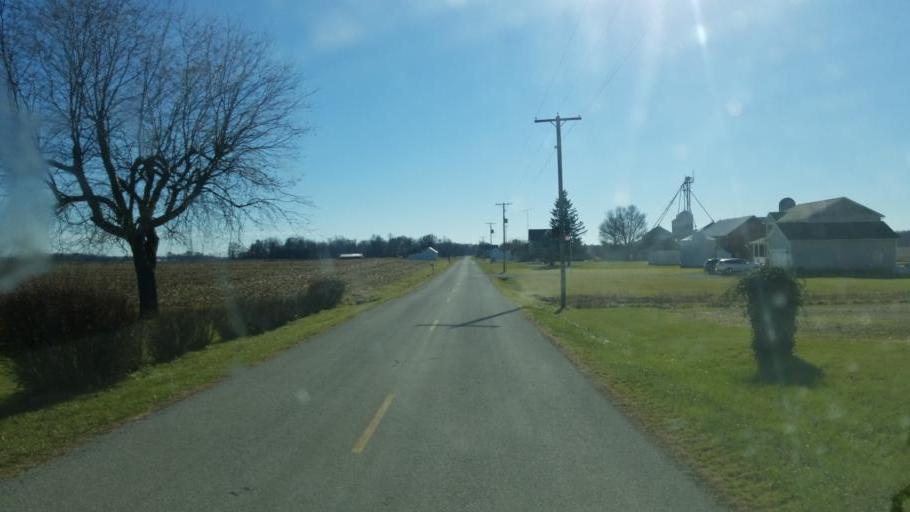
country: US
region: Ohio
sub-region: Crawford County
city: Galion
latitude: 40.8220
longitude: -82.8375
